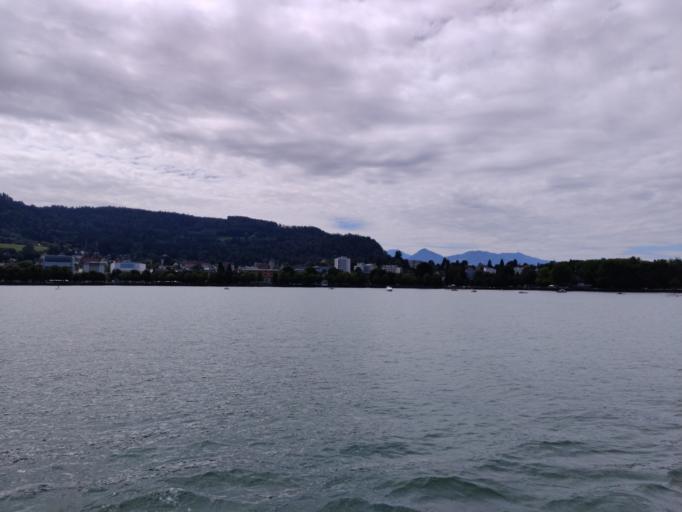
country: AT
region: Vorarlberg
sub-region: Politischer Bezirk Bregenz
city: Bregenz
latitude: 47.5094
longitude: 9.7416
